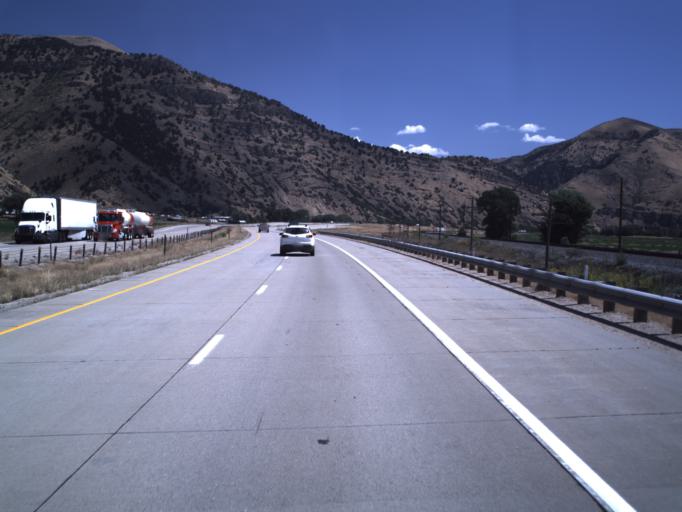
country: US
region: Utah
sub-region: Morgan County
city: Morgan
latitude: 41.0495
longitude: -111.6342
